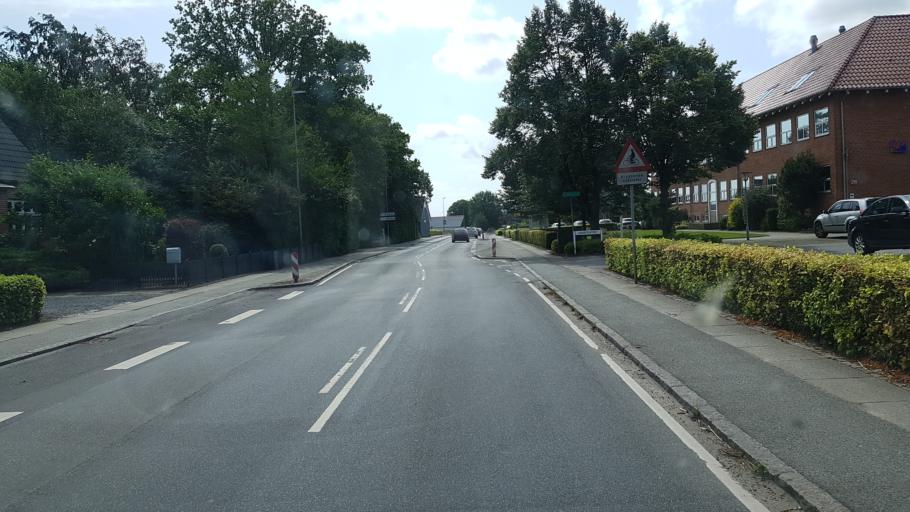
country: DK
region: South Denmark
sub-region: Vejen Kommune
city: Vejen
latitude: 55.5684
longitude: 9.1362
